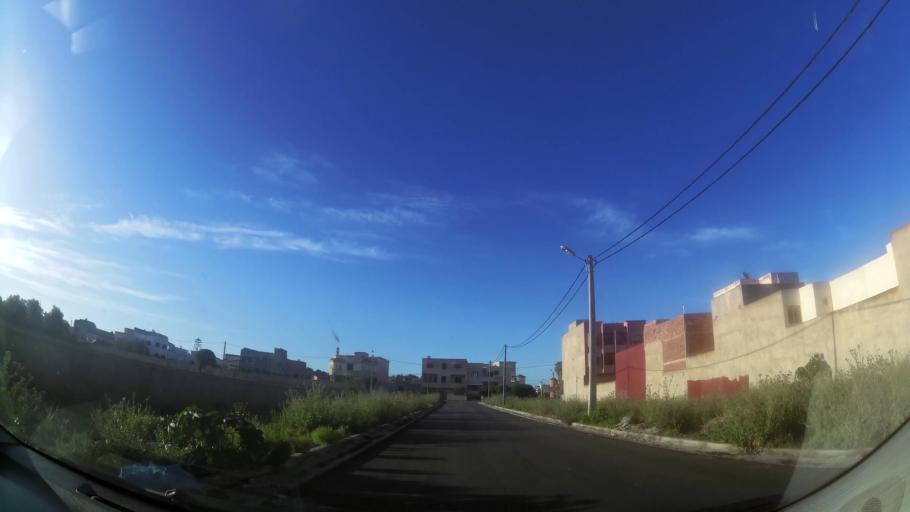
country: MA
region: Oriental
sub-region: Berkane-Taourirt
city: Madagh
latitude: 35.0837
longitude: -2.2400
